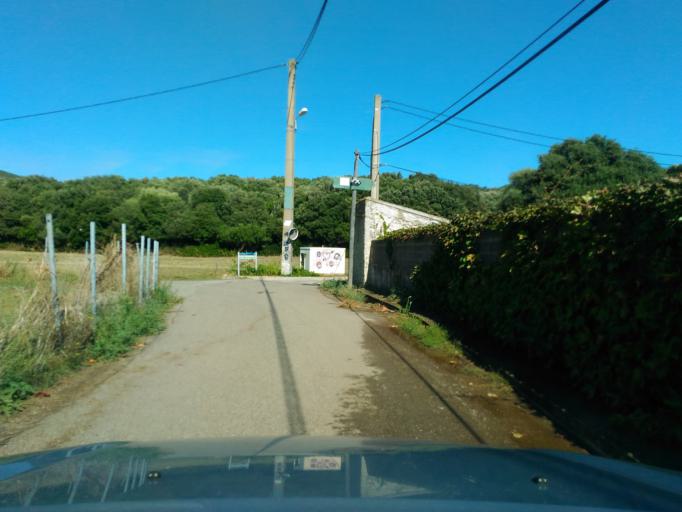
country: FR
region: Corsica
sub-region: Departement de la Haute-Corse
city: Brando
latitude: 42.9606
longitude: 9.4471
